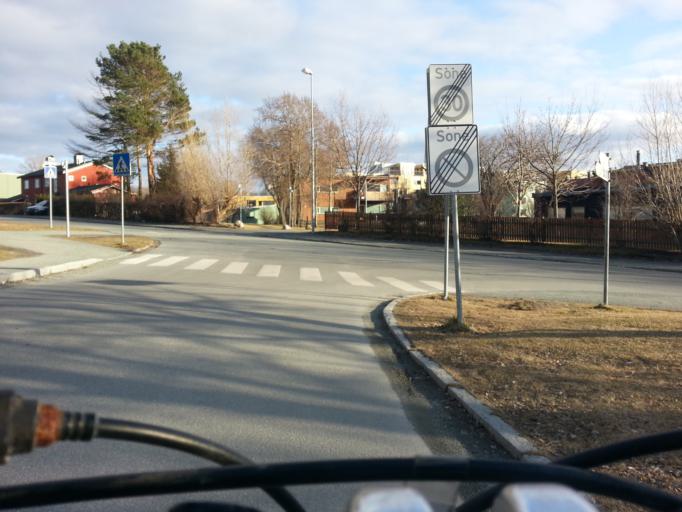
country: NO
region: Sor-Trondelag
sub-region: Trondheim
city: Trondheim
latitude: 63.4499
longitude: 10.4437
